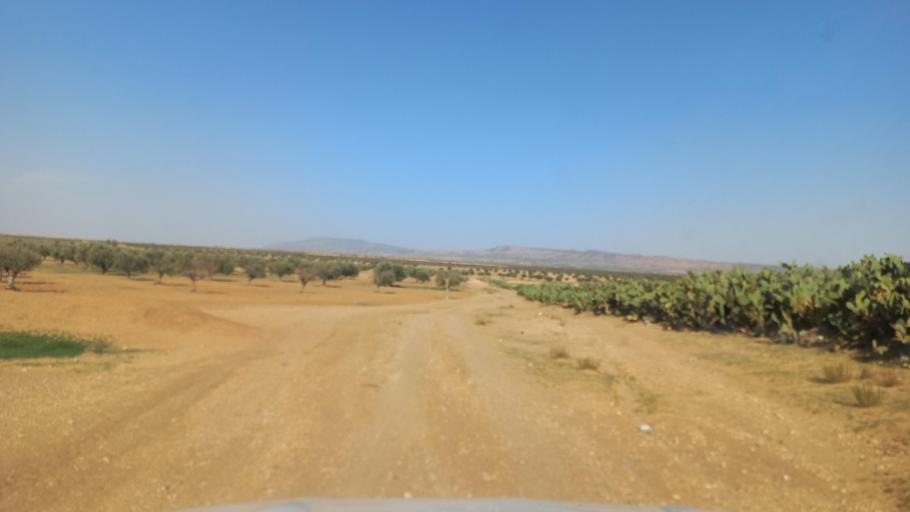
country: TN
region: Al Qasrayn
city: Sbiba
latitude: 35.3222
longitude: 9.0217
